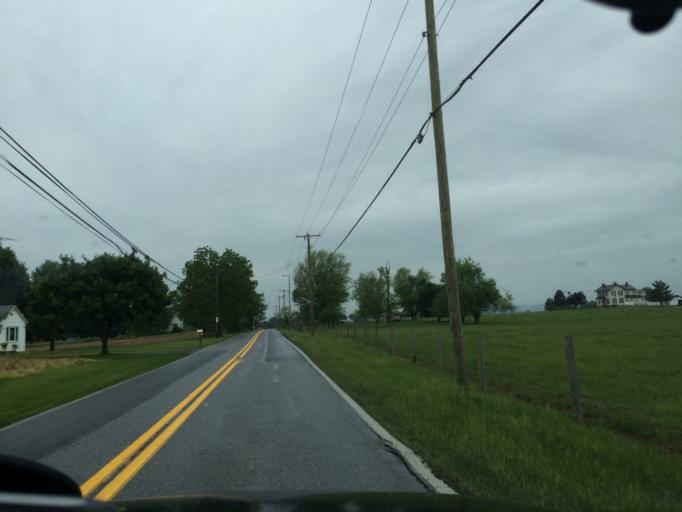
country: US
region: Maryland
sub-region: Carroll County
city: Taneytown
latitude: 39.5930
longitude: -77.1898
